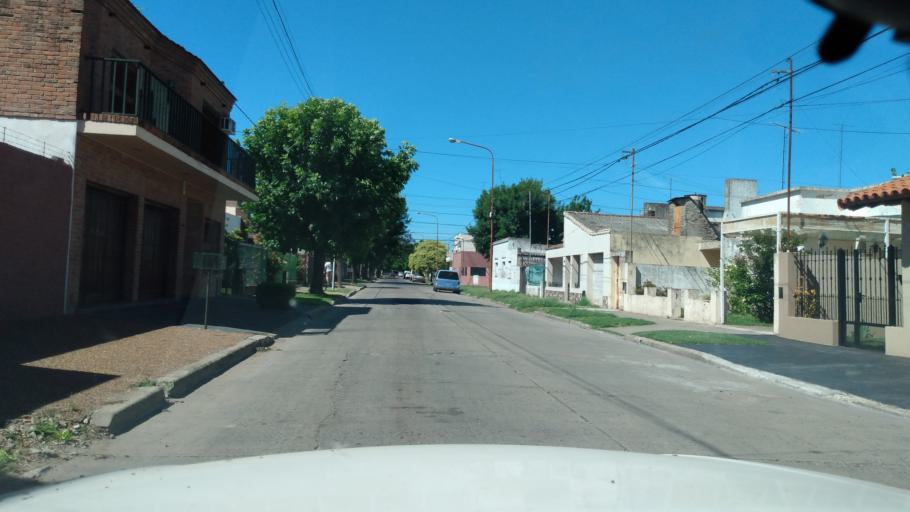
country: AR
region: Buenos Aires
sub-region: Partido de Lujan
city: Lujan
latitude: -34.5623
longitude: -59.1069
